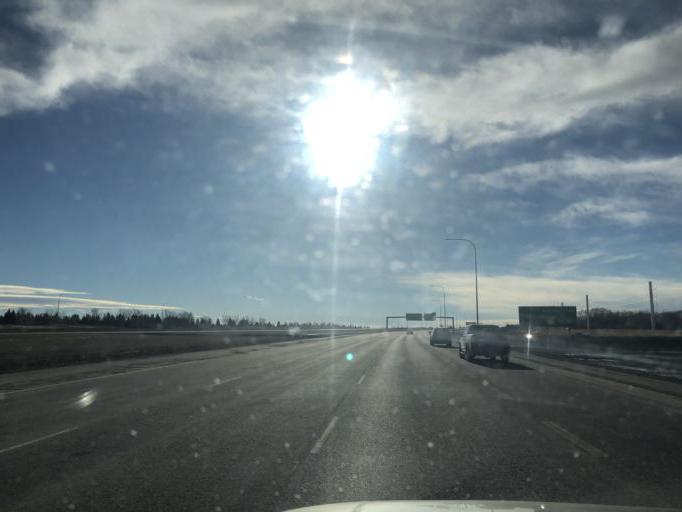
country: CA
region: Alberta
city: Calgary
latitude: 50.9633
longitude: -114.1467
